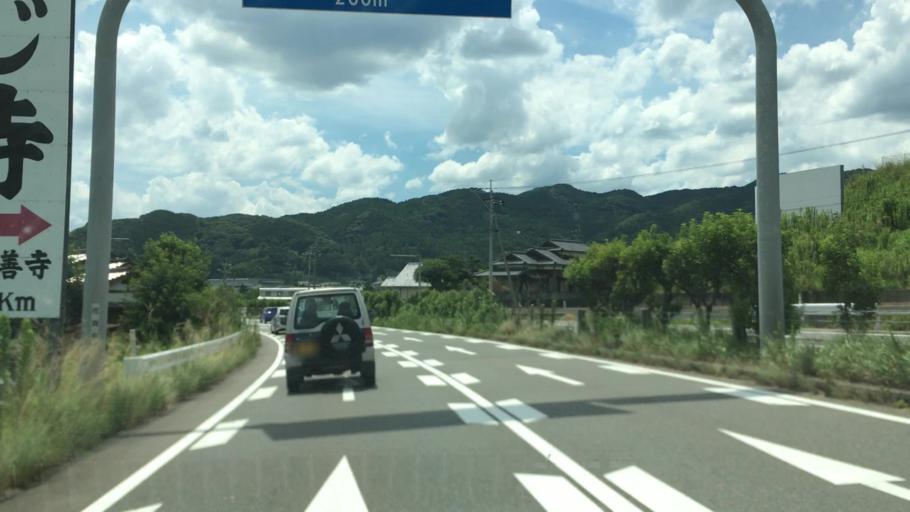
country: JP
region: Saga Prefecture
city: Tosu
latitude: 33.4221
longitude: 130.5122
